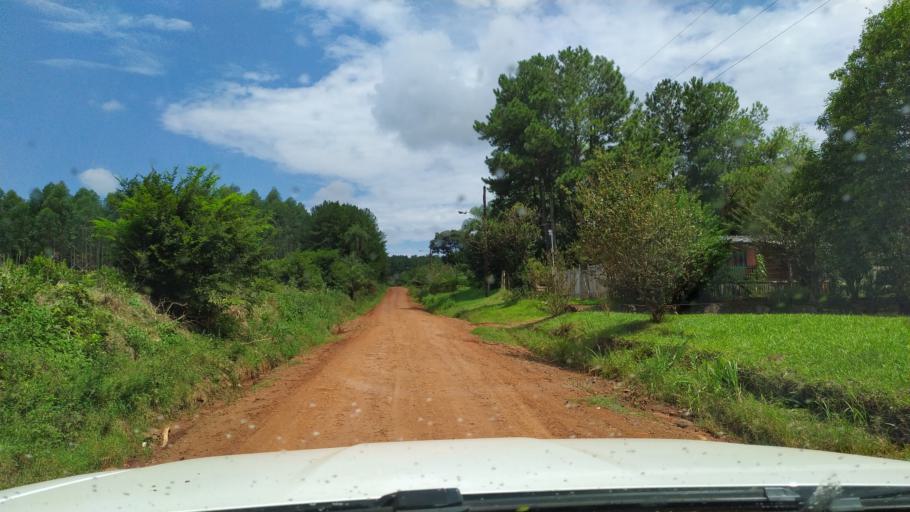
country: AR
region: Misiones
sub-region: Departamento de Eldorado
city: Eldorado
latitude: -26.4969
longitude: -54.5881
